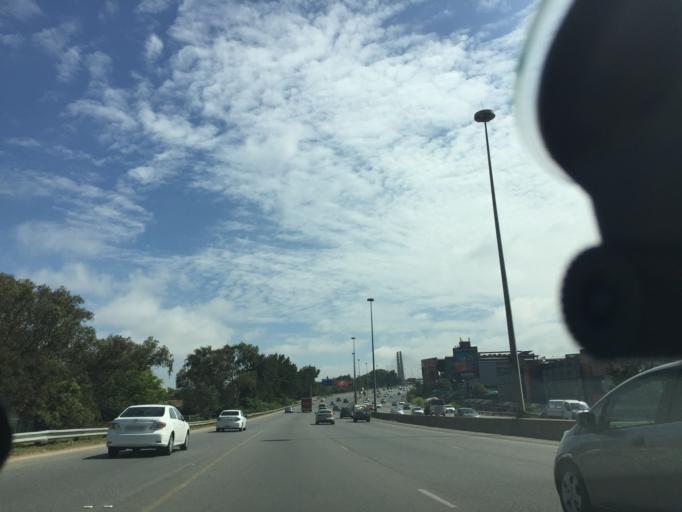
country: ZA
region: Gauteng
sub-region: City of Johannesburg Metropolitan Municipality
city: Modderfontein
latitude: -26.1045
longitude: 28.0775
